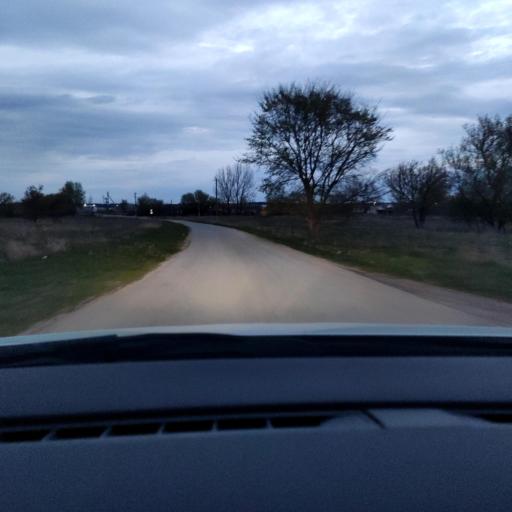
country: RU
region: Lipetsk
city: Donskoye
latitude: 52.6770
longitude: 38.9176
